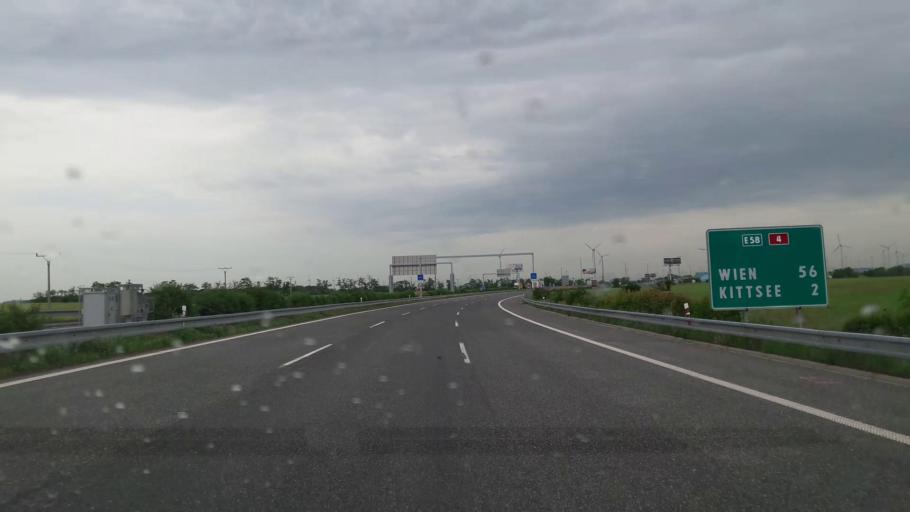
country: AT
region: Burgenland
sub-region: Politischer Bezirk Neusiedl am See
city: Kittsee
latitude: 48.0704
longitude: 17.0870
